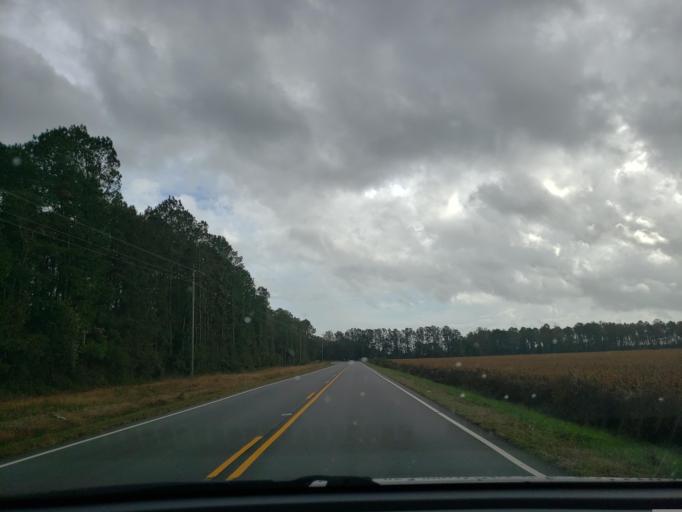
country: US
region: North Carolina
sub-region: Duplin County
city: Beulaville
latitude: 34.8410
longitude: -77.8646
